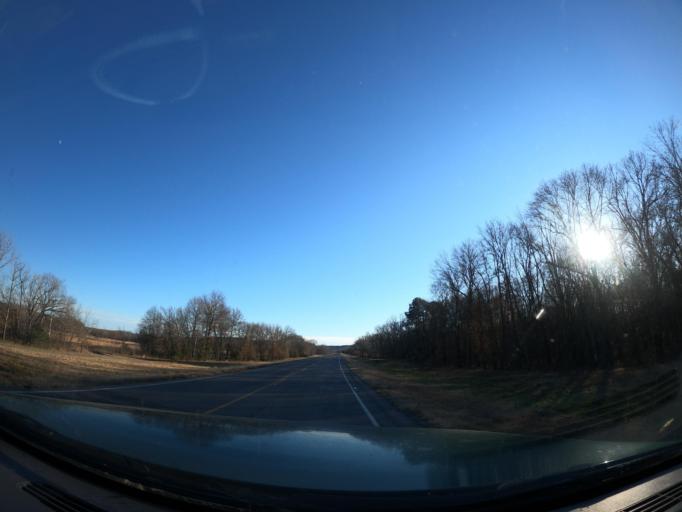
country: US
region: Oklahoma
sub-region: Latimer County
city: Wilburton
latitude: 34.9485
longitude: -95.3413
